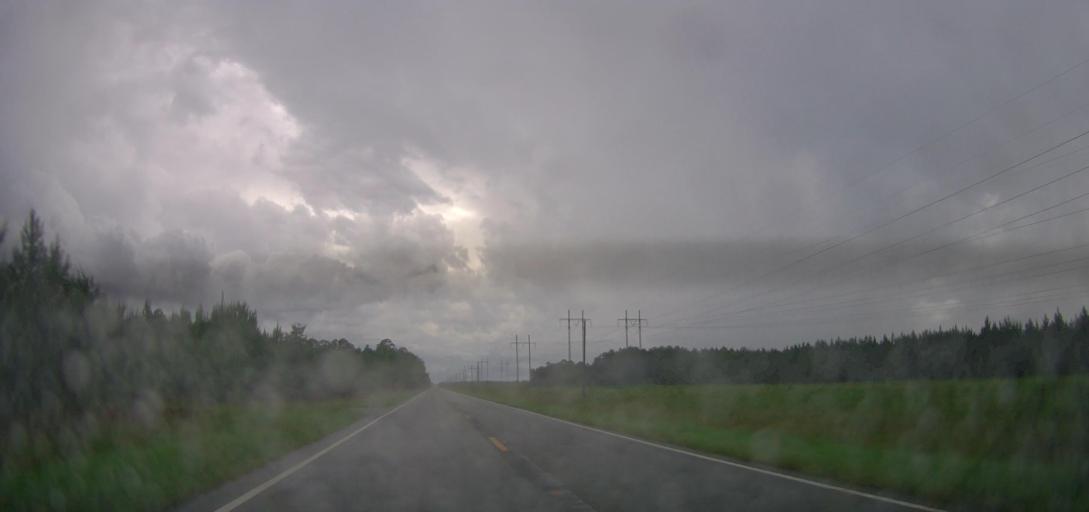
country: US
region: Georgia
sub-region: Brantley County
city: Nahunta
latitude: 31.3398
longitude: -81.8450
